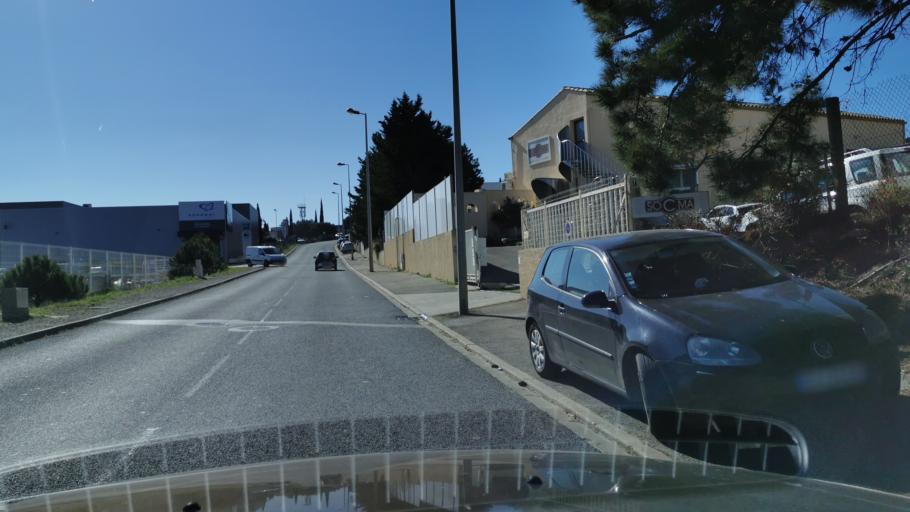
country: FR
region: Languedoc-Roussillon
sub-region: Departement de l'Aude
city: Narbonne
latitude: 43.1545
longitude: 2.9787
